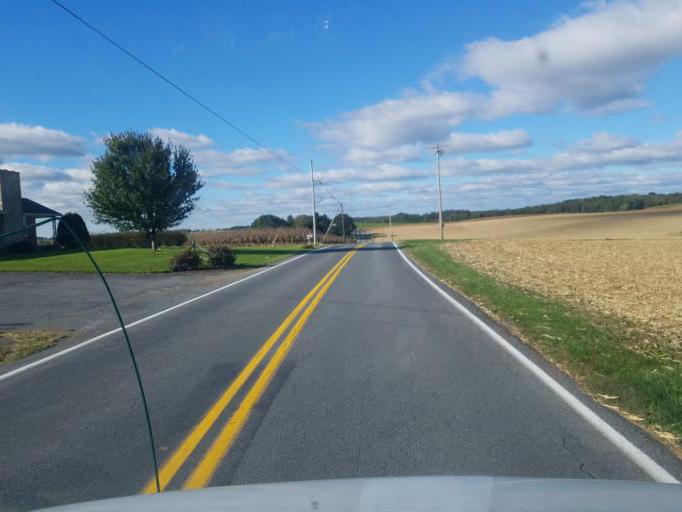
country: US
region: Pennsylvania
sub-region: Franklin County
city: Guilford Siding
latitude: 39.8582
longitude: -77.5967
